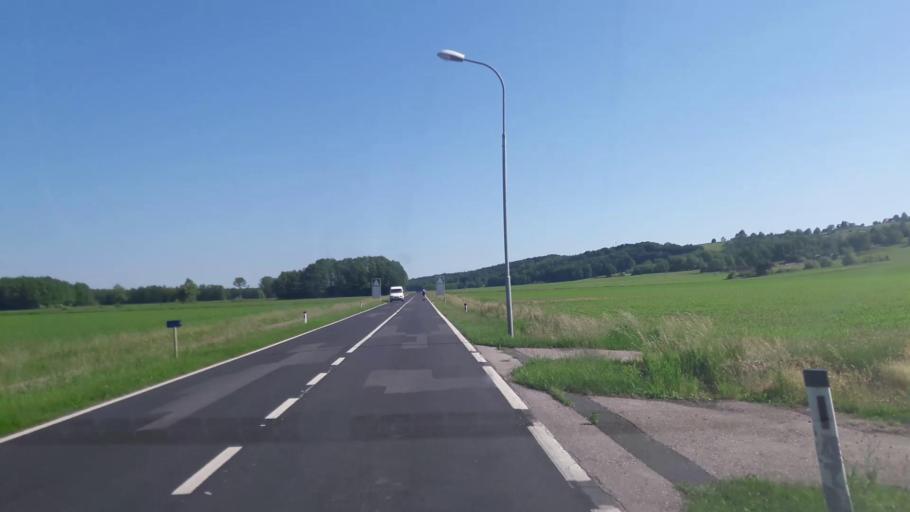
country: AT
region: Burgenland
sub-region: Politischer Bezirk Jennersdorf
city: Deutsch Kaltenbrunn
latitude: 47.0957
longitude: 16.1065
